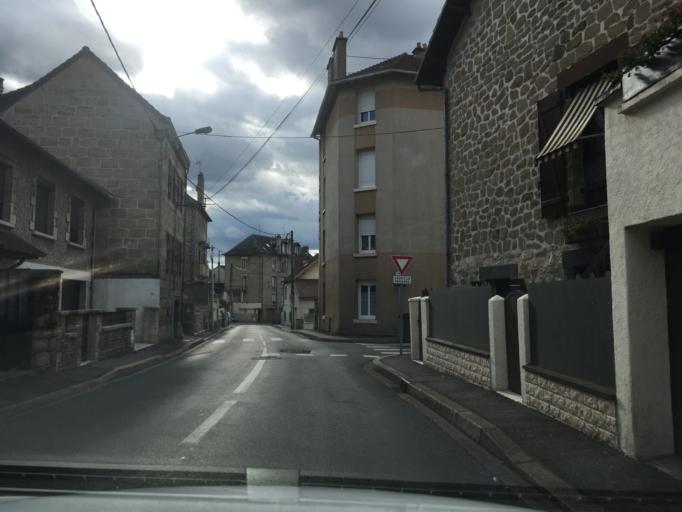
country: FR
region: Limousin
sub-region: Departement de la Correze
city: Brive-la-Gaillarde
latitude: 45.1518
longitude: 1.5440
